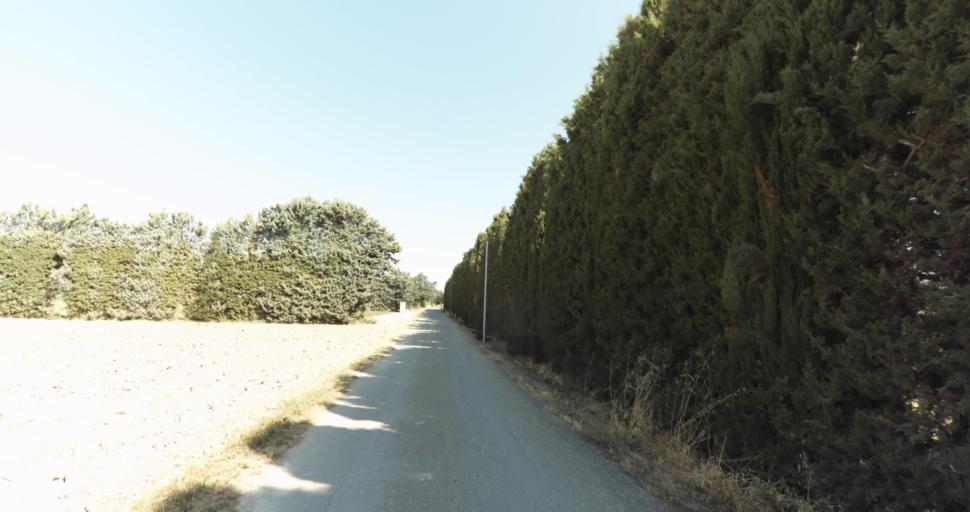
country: FR
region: Provence-Alpes-Cote d'Azur
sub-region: Departement du Vaucluse
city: Monteux
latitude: 44.0075
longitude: 4.9968
